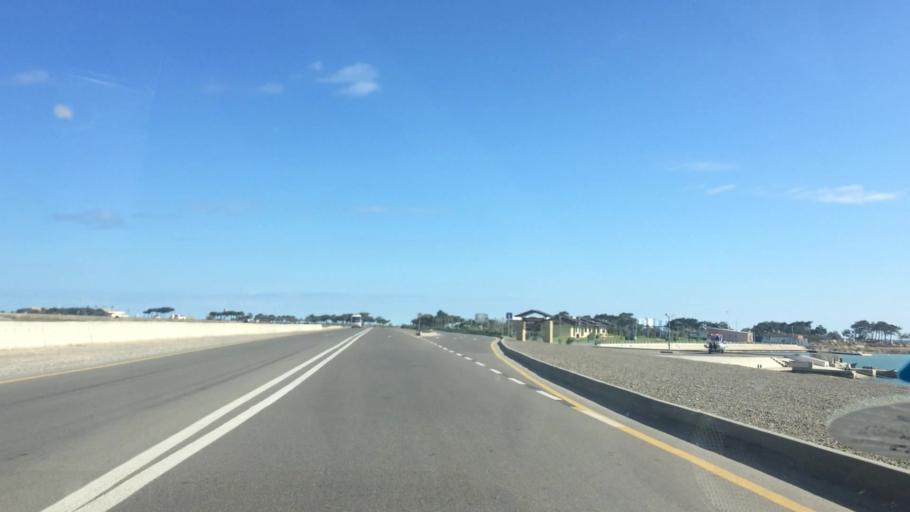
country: AZ
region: Baki
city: Pirallahi
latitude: 40.4090
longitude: 50.3506
